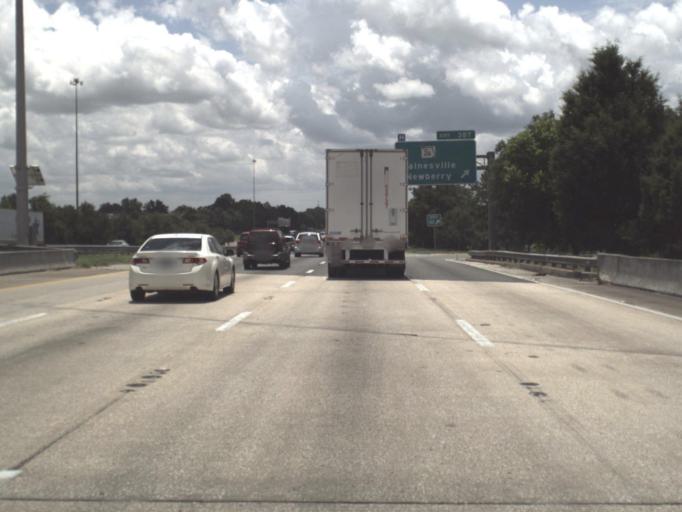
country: US
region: Florida
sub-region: Alachua County
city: Alachua
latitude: 29.6596
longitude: -82.4191
